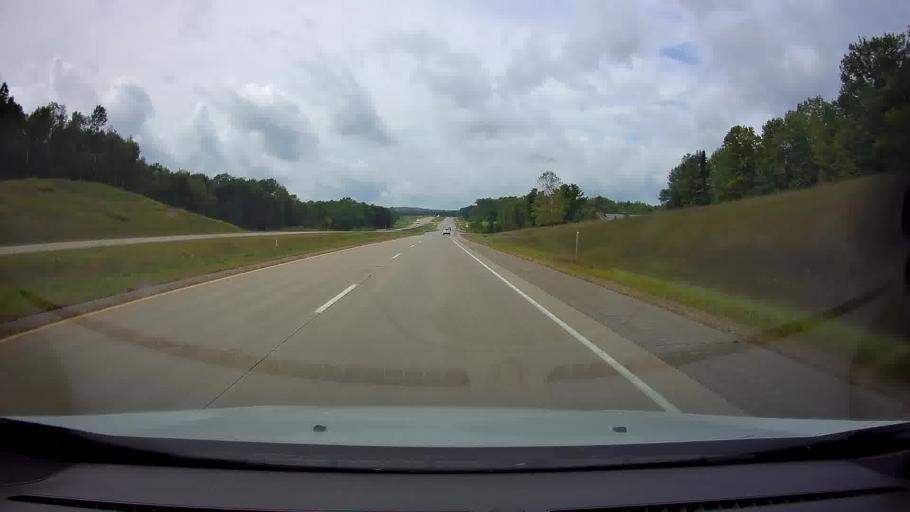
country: US
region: Wisconsin
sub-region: Shawano County
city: Wittenberg
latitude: 44.8039
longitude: -89.0129
